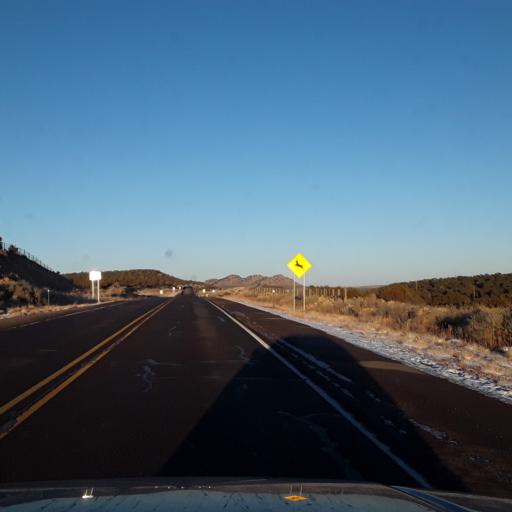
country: US
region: New Mexico
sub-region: Lincoln County
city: Carrizozo
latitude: 34.2554
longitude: -105.5924
